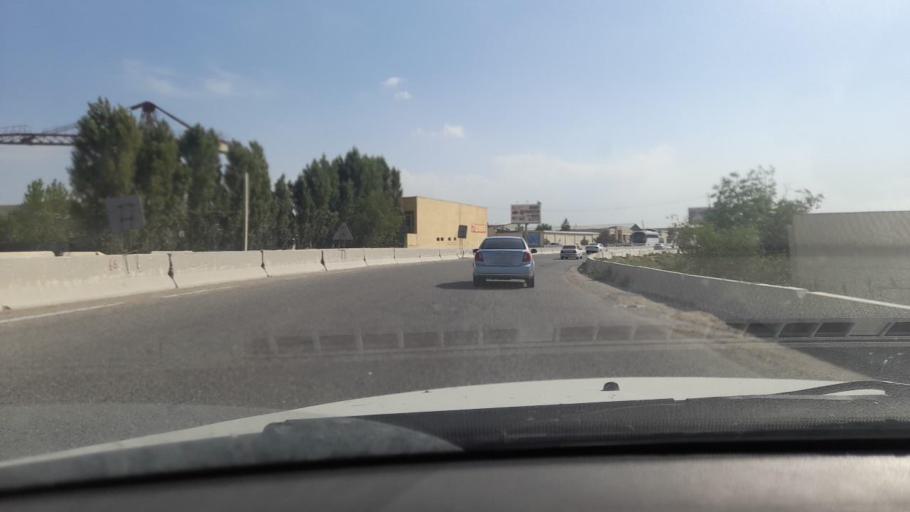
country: UZ
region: Samarqand
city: Samarqand
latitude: 39.6955
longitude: 67.0190
